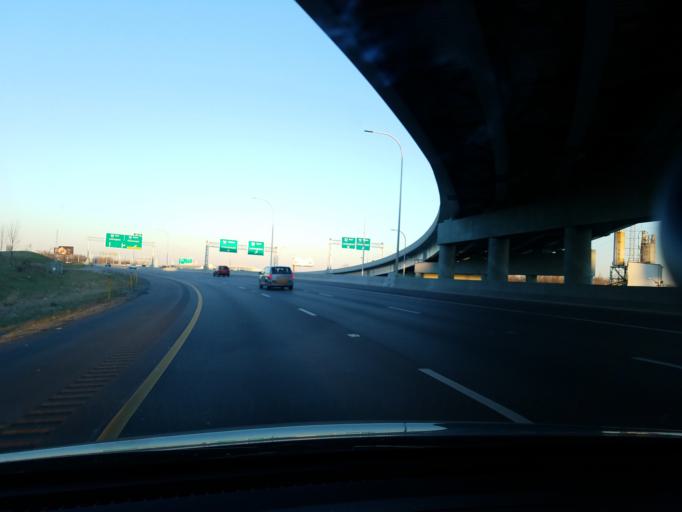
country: US
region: Indiana
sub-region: Clark County
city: Jeffersonville
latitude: 38.2583
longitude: -85.7401
